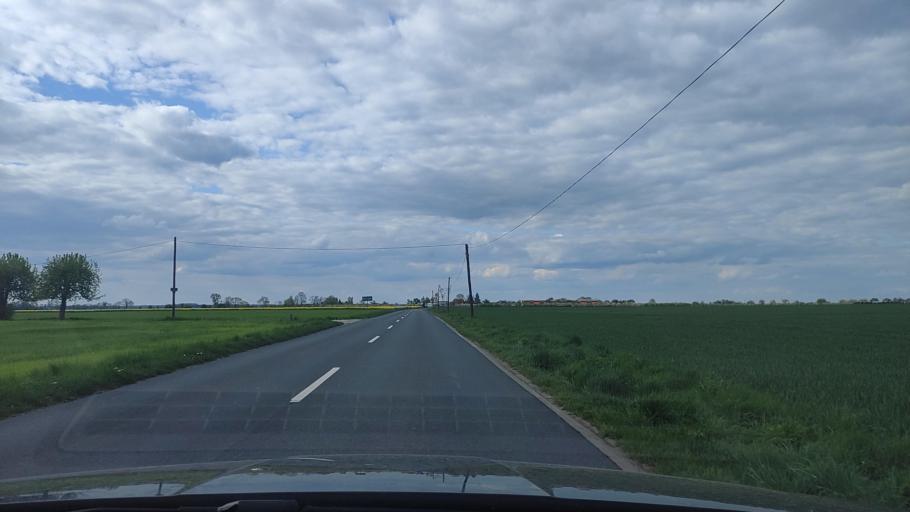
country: PL
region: Greater Poland Voivodeship
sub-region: Powiat poznanski
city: Kostrzyn
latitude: 52.4070
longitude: 17.1570
